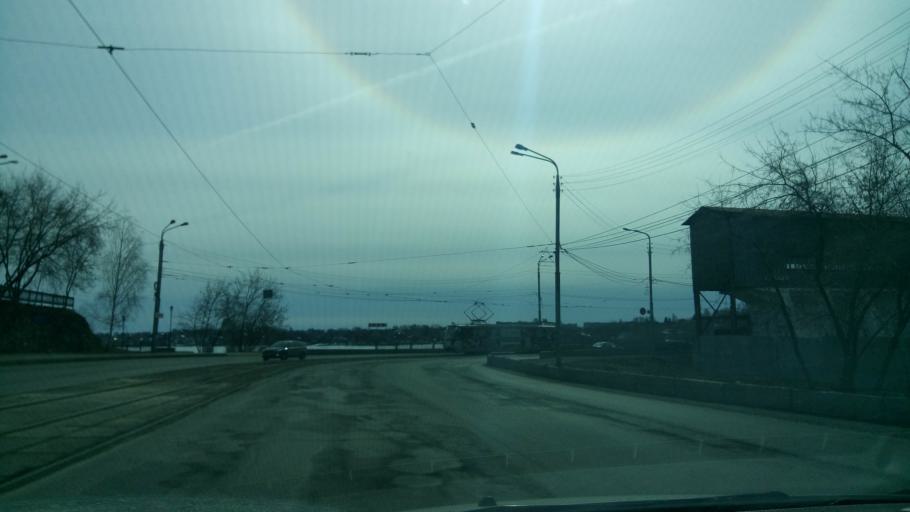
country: RU
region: Sverdlovsk
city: Nizhniy Tagil
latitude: 57.9051
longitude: 59.9495
